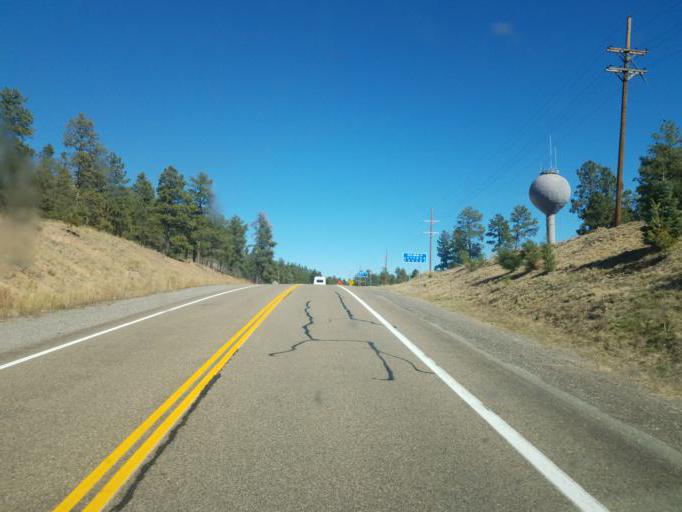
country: US
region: New Mexico
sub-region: Los Alamos County
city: Los Alamos
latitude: 35.8683
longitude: -106.3514
